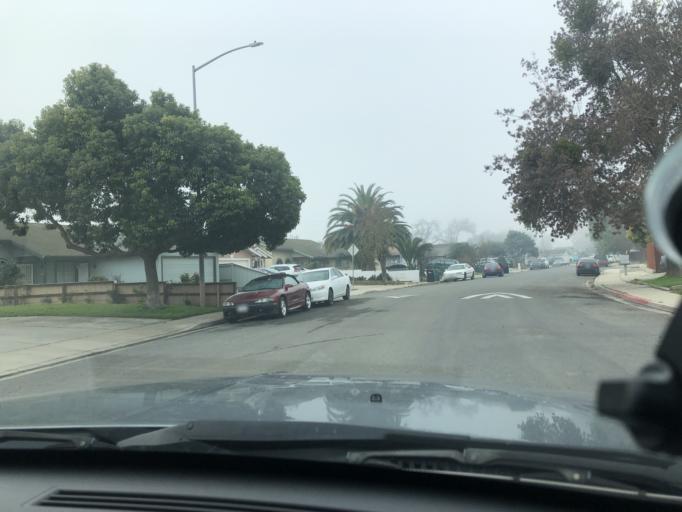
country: US
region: California
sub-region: Monterey County
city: King City
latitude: 36.2043
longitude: -121.1414
